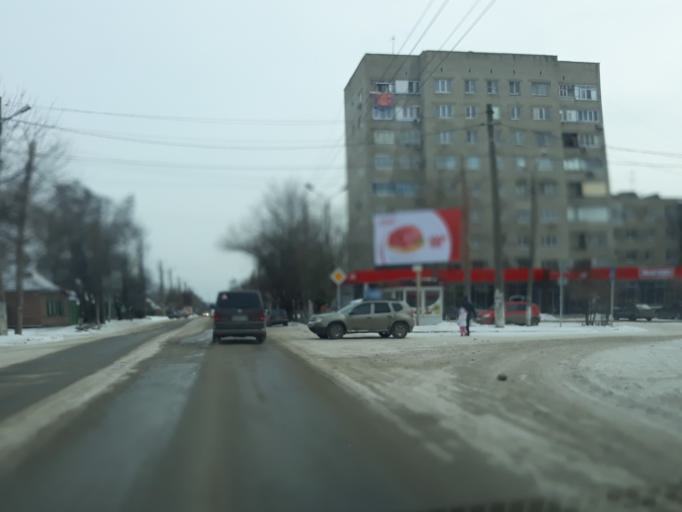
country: RU
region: Rostov
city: Taganrog
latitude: 47.2203
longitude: 38.8916
